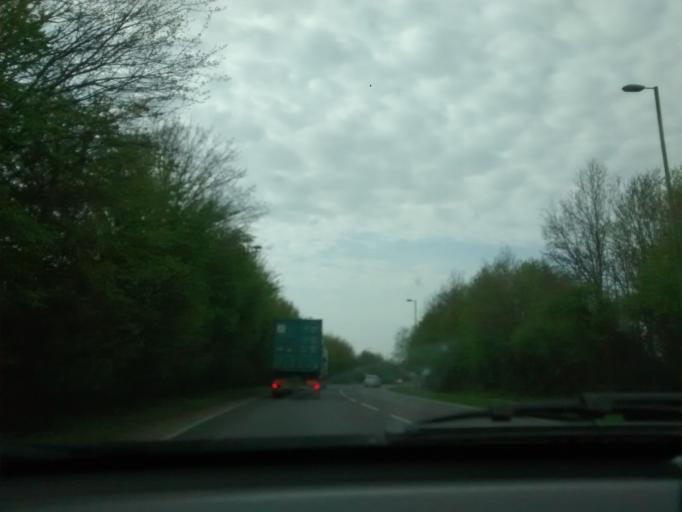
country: GB
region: England
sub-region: Oxfordshire
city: Bicester
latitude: 51.8943
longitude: -1.1280
